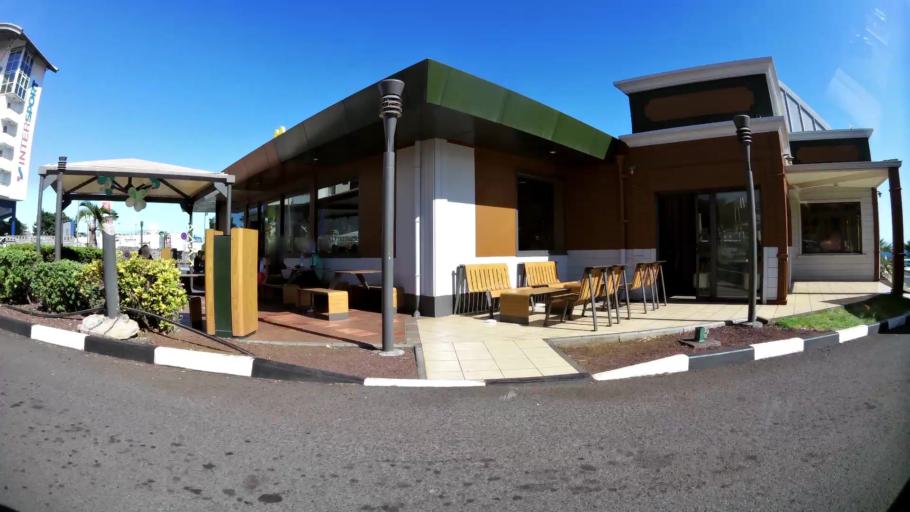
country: RE
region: Reunion
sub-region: Reunion
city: Saint-Pierre
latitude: -21.3293
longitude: 55.4724
